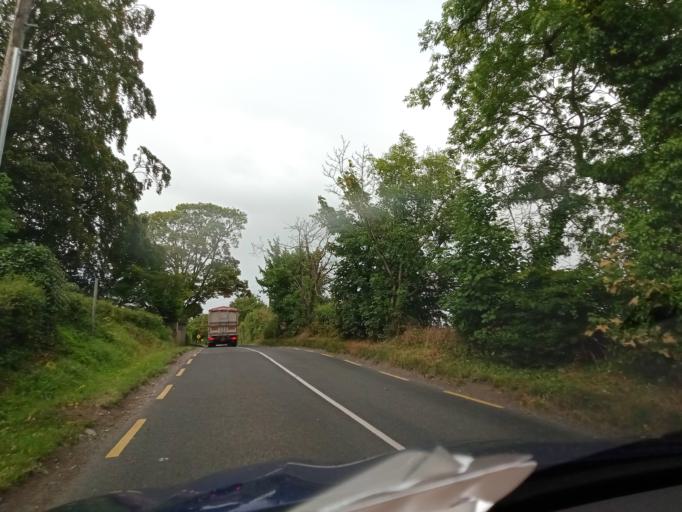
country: IE
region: Leinster
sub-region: Laois
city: Portlaoise
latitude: 53.0174
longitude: -7.2820
